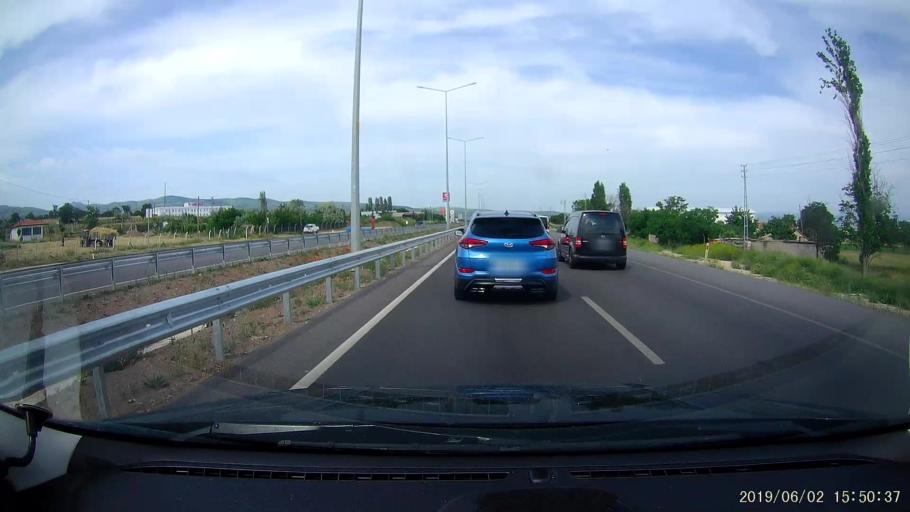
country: TR
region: Amasya
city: Merzifon
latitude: 40.8610
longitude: 35.4830
